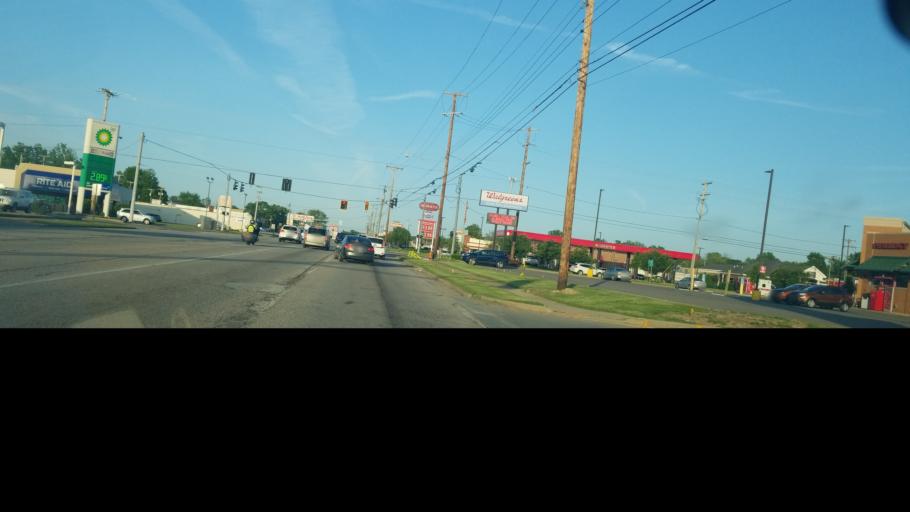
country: US
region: Ohio
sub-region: Mahoning County
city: Austintown
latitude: 41.0996
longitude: -80.7650
